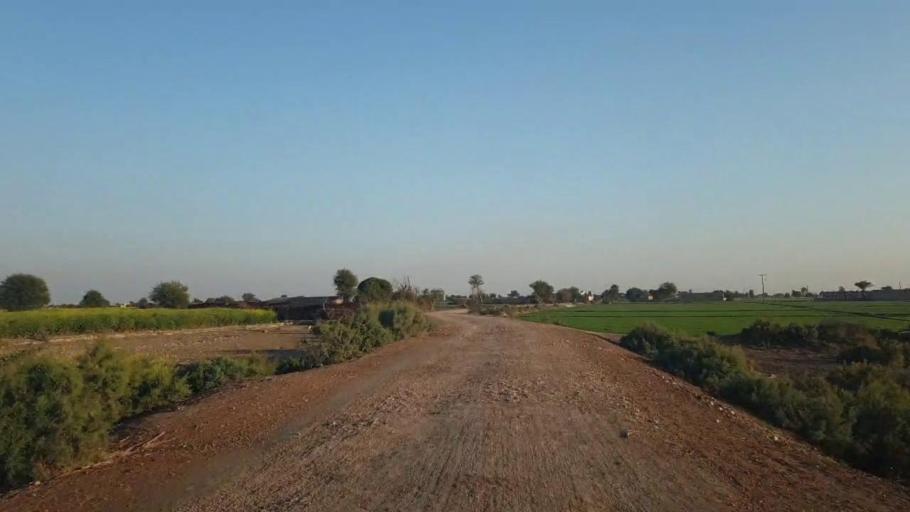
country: PK
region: Sindh
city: Khadro
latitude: 26.0752
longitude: 68.6830
